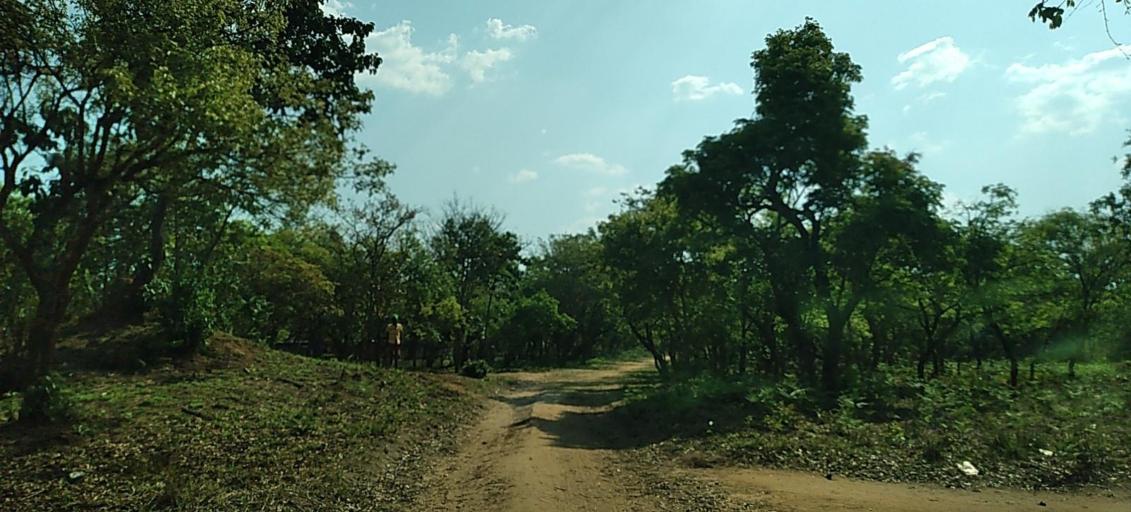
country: ZM
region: North-Western
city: Mwinilunga
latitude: -11.2995
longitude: 24.8522
